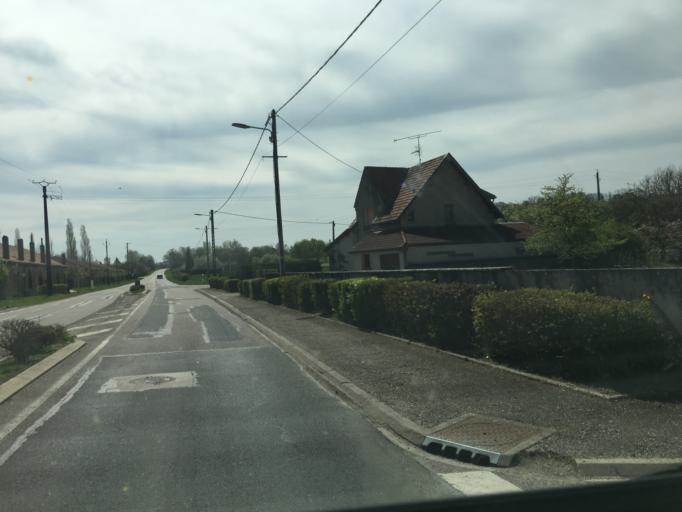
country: FR
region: Lorraine
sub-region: Departement de la Meuse
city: Lerouville
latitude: 48.8216
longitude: 5.5114
